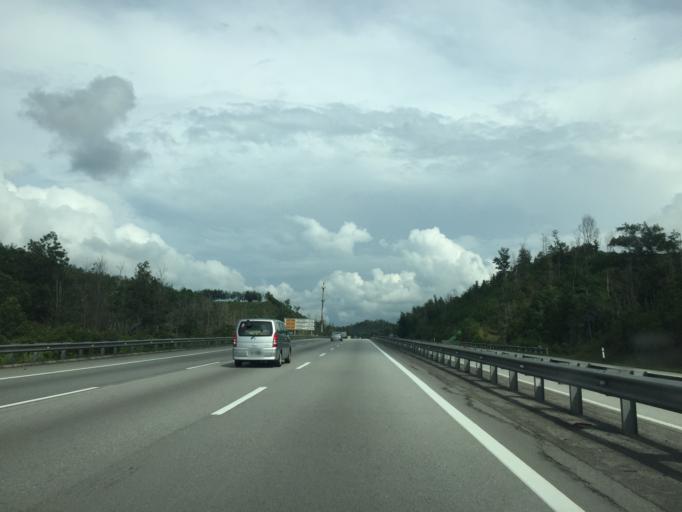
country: MY
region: Selangor
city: Batang Berjuntai
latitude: 3.5308
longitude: 101.5218
